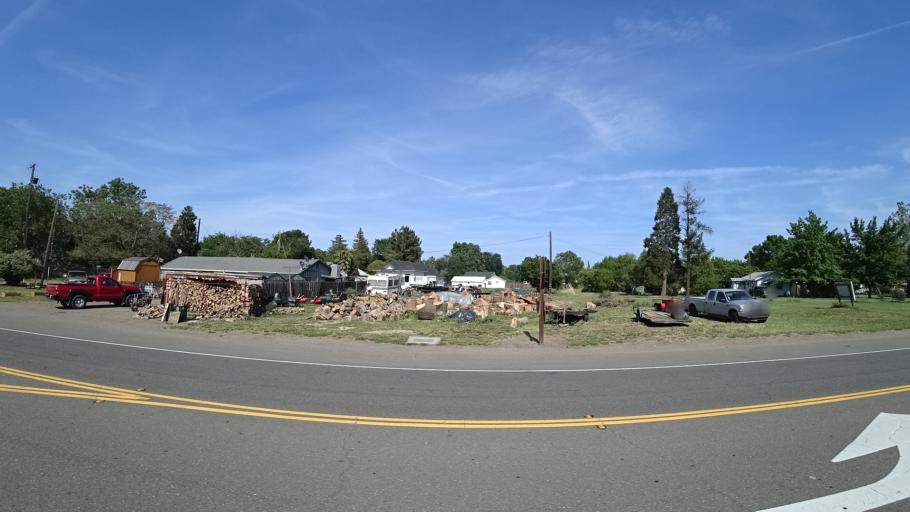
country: US
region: California
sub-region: Tehama County
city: Los Molinos
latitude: 40.0198
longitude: -122.0995
